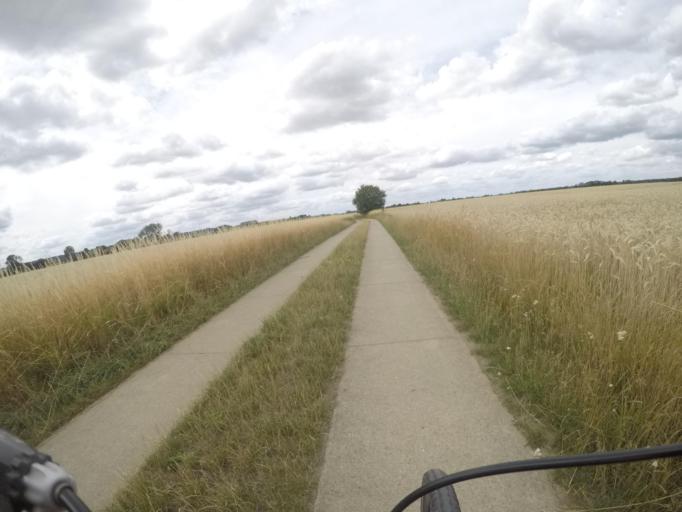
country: DE
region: Lower Saxony
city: Hitzacker
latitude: 53.1881
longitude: 11.0221
